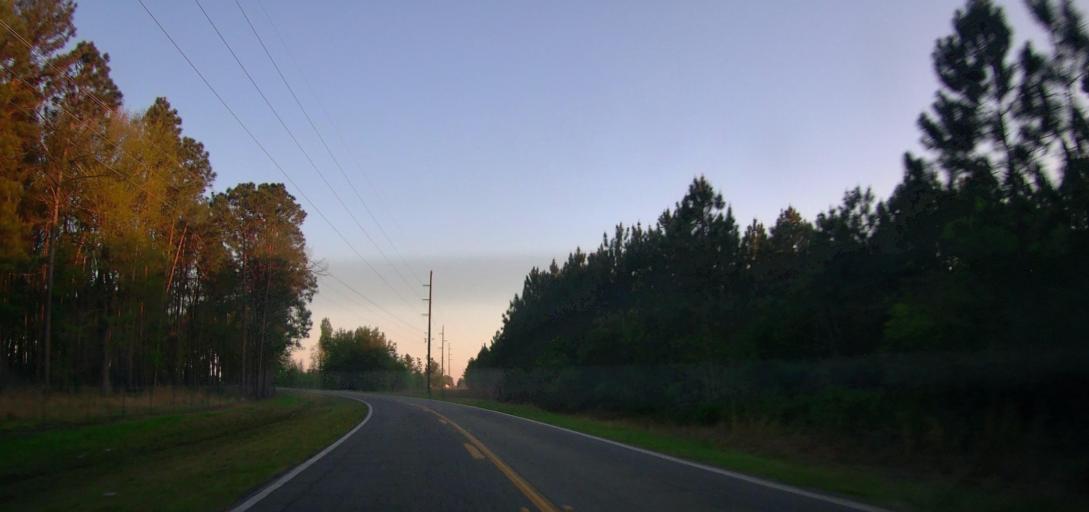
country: US
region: Georgia
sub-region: Ben Hill County
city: Fitzgerald
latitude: 31.7599
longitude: -83.3549
